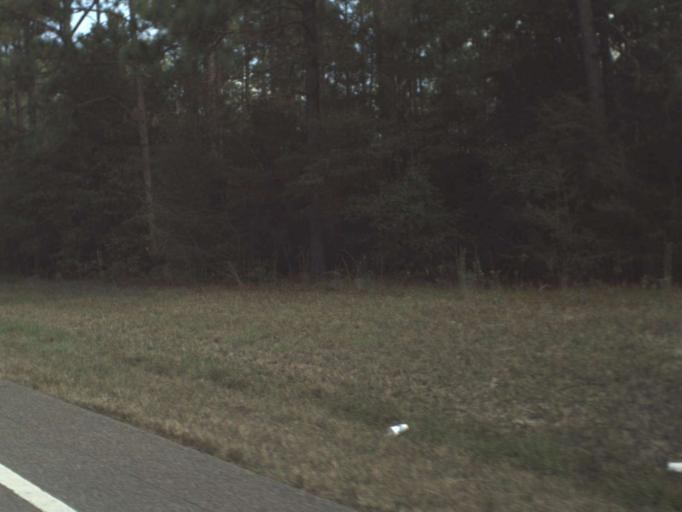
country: US
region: Florida
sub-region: Walton County
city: DeFuniak Springs
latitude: 30.8965
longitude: -86.1291
